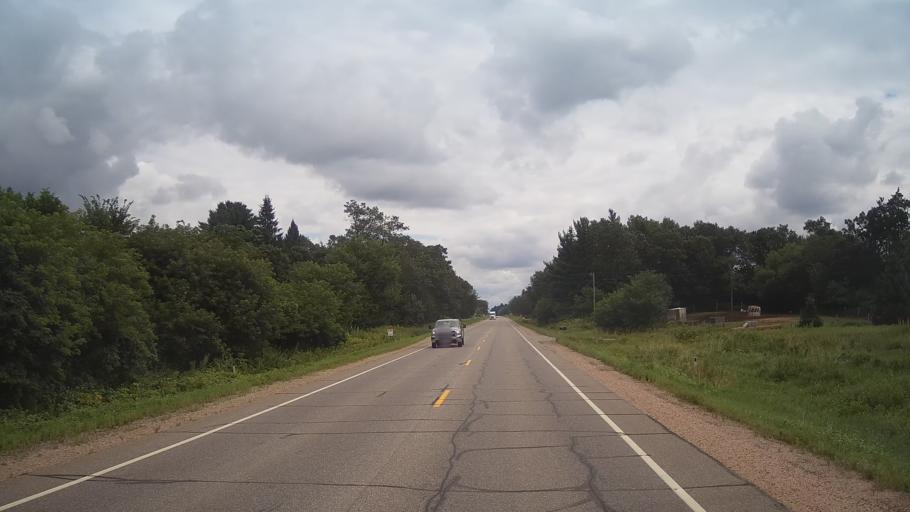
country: US
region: Wisconsin
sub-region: Adams County
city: Friendship
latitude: 44.0395
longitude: -89.9475
